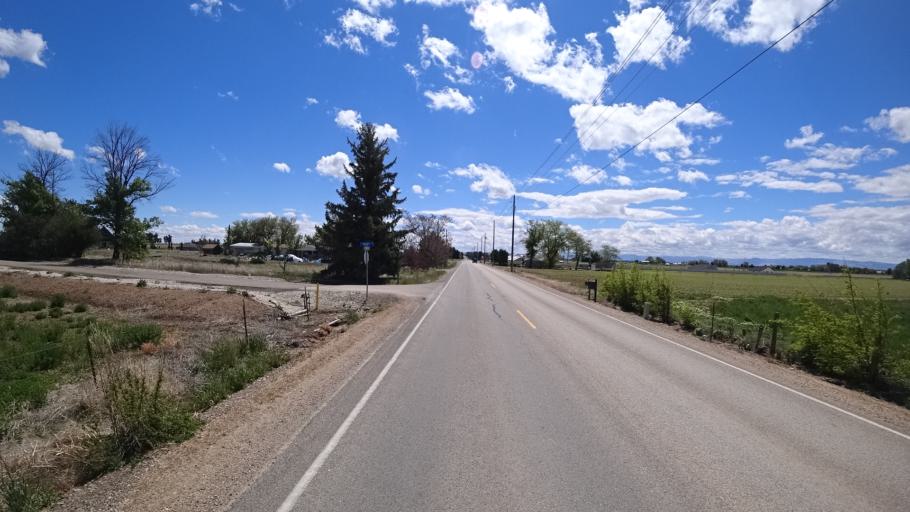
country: US
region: Idaho
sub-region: Ada County
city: Kuna
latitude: 43.5540
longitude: -116.4337
